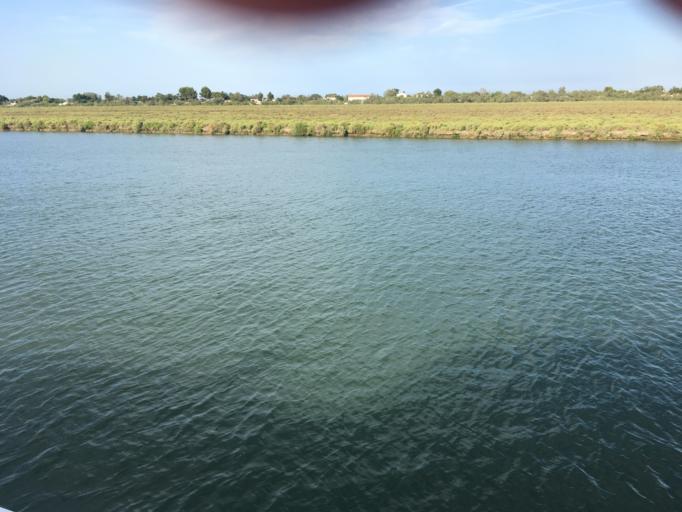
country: FR
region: Provence-Alpes-Cote d'Azur
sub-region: Departement des Bouches-du-Rhone
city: Saintes-Maries-de-la-Mer
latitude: 43.4689
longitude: 4.3890
